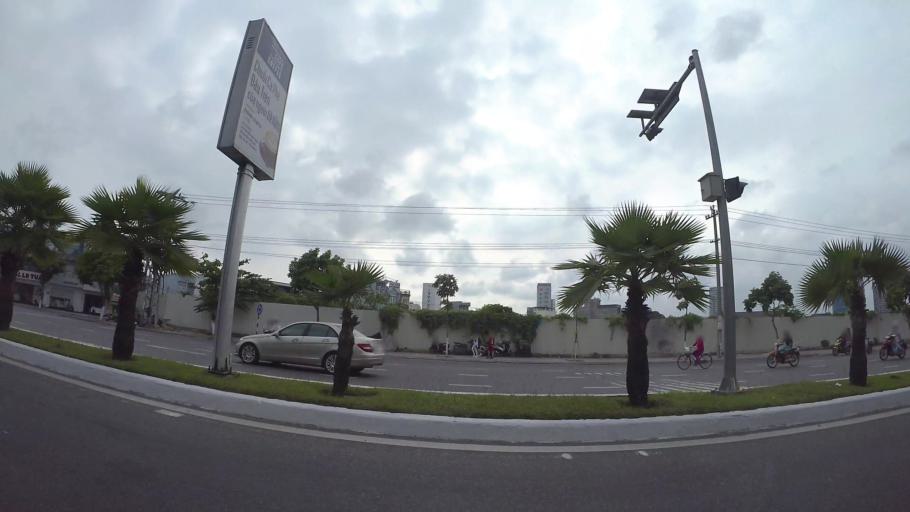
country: VN
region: Da Nang
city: Son Tra
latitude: 16.0686
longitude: 108.2322
